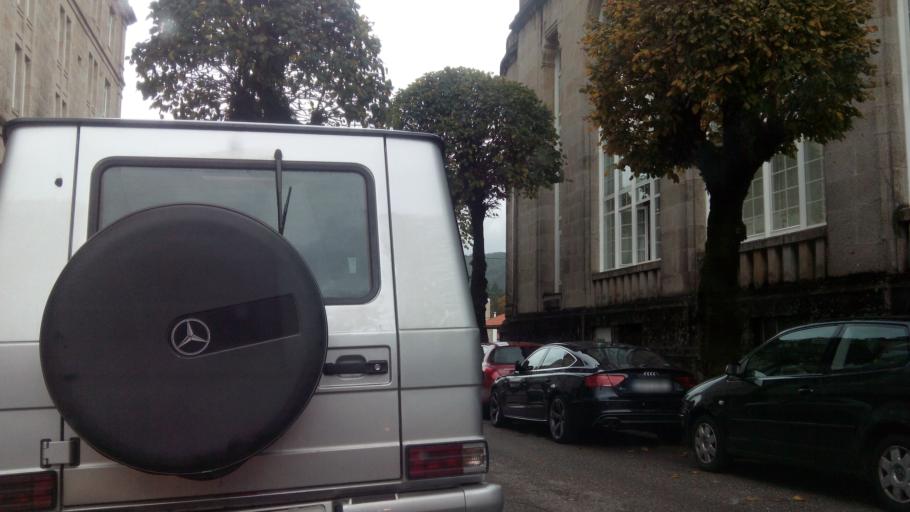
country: ES
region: Galicia
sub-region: Provincia de Pontevedra
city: Mondariz-Balneario
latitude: 42.2272
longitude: -8.4663
